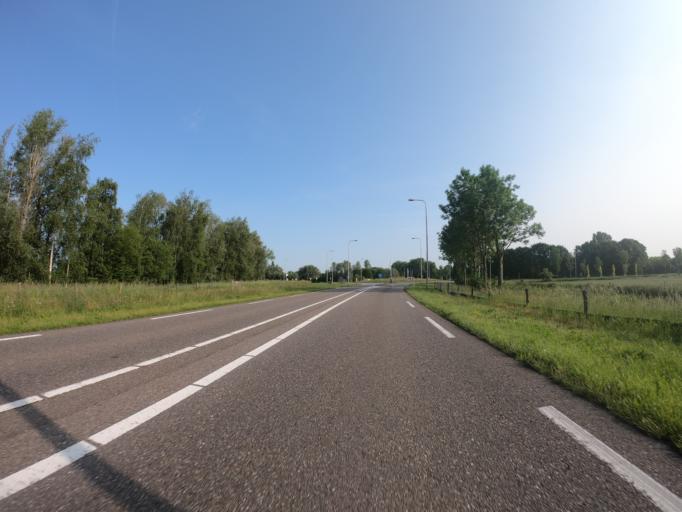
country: NL
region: North Brabant
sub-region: Gemeente Landerd
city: Reek
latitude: 51.7719
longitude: 5.6670
